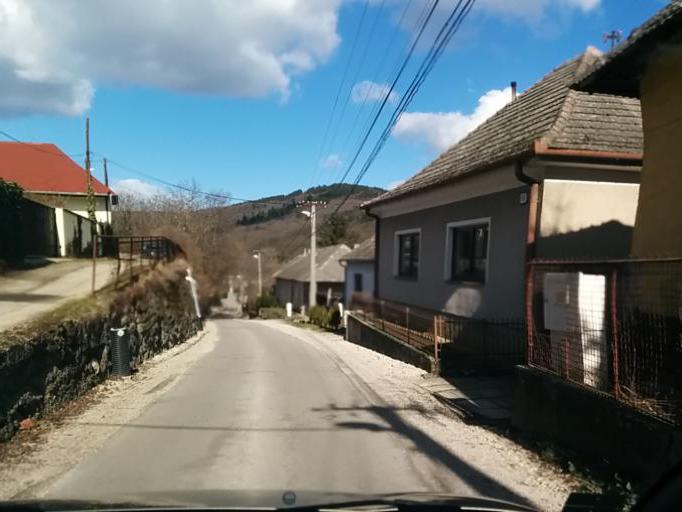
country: SK
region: Nitriansky
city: Cachtice
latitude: 48.7176
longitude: 17.7862
